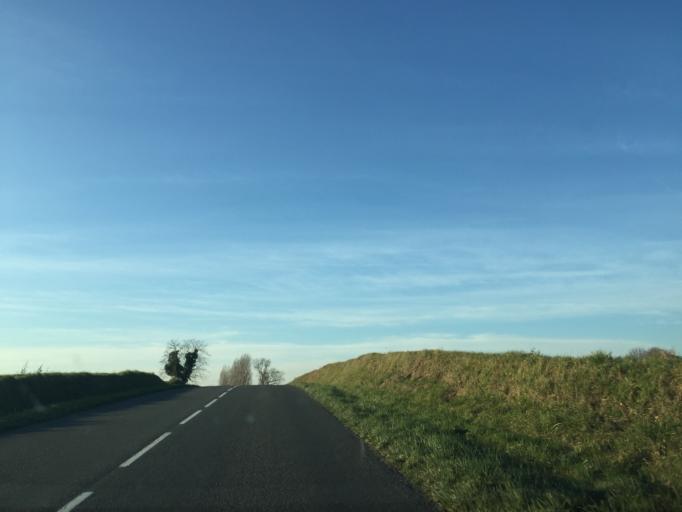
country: FR
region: Aquitaine
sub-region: Departement de la Dordogne
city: Saint-Aulaye
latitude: 45.2792
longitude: 0.1293
